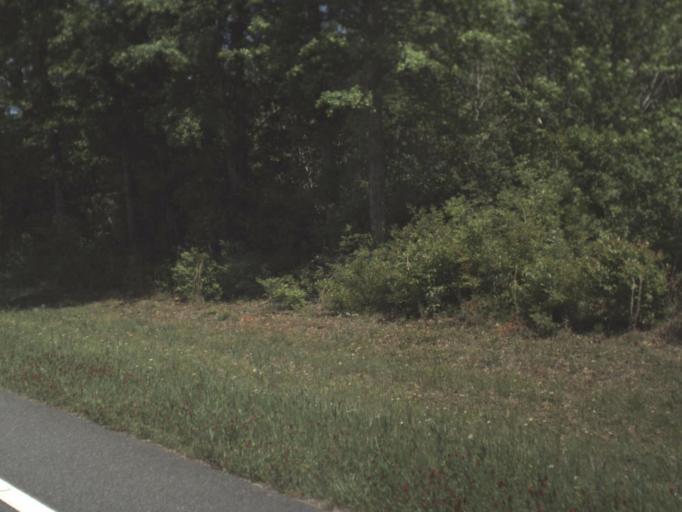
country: US
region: Alabama
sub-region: Escambia County
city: East Brewton
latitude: 30.9761
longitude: -87.0455
